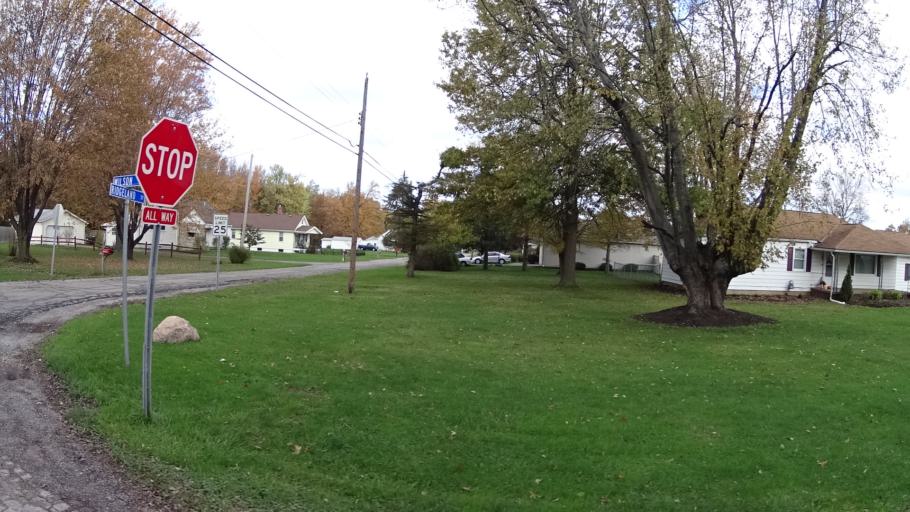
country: US
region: Ohio
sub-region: Lorain County
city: Sheffield
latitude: 41.4208
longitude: -82.1206
